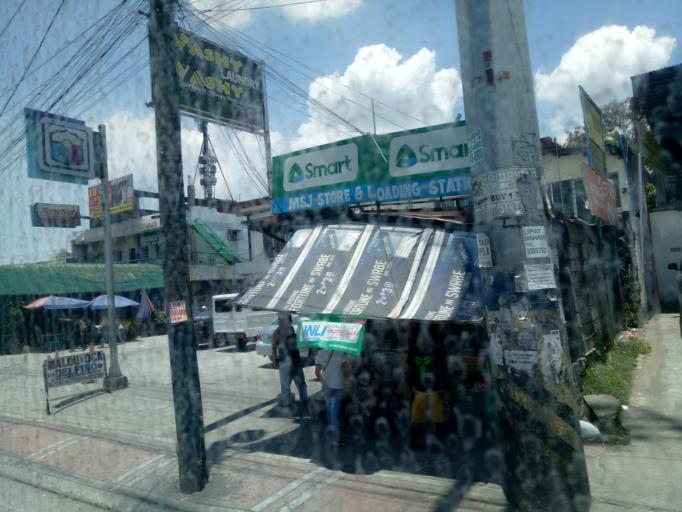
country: PH
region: Calabarzon
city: Bagong Pagasa
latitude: 14.7315
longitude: 121.0481
